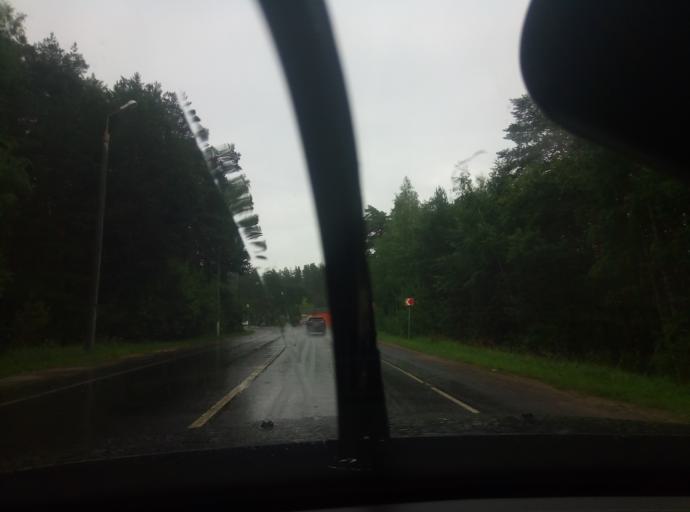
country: RU
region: Moskovskaya
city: Protvino
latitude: 54.8760
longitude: 37.2451
